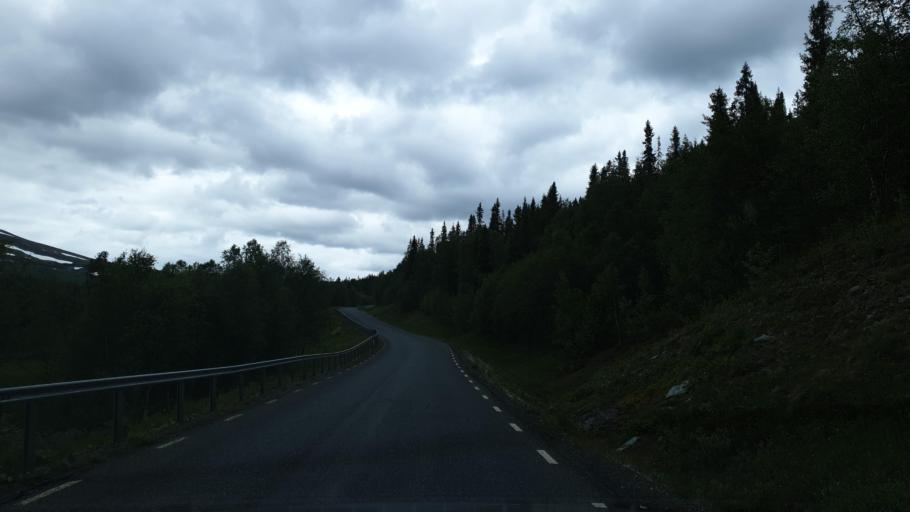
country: SE
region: Vaesterbotten
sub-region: Vilhelmina Kommun
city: Sjoberg
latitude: 65.2771
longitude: 15.3190
